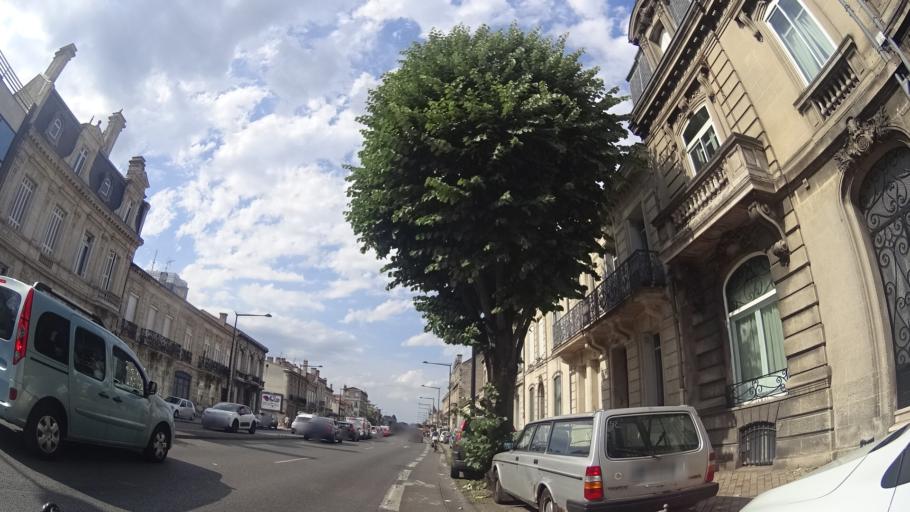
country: FR
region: Aquitaine
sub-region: Departement de la Gironde
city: Bordeaux
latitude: 44.8390
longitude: -0.5991
